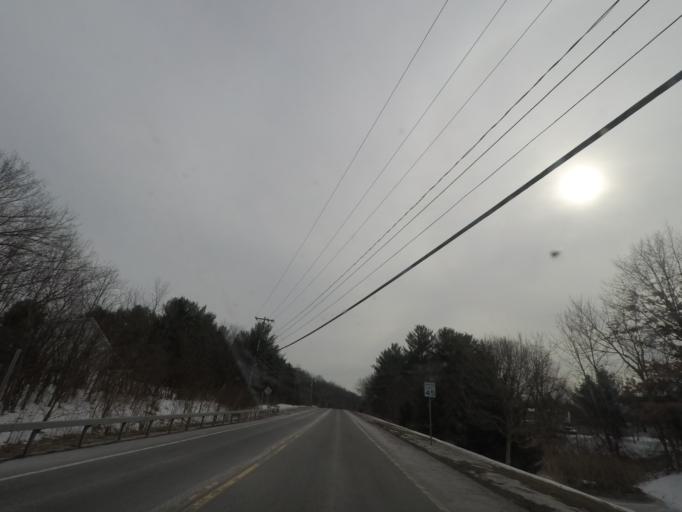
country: US
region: New York
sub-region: Albany County
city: Voorheesville
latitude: 42.6702
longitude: -73.9131
